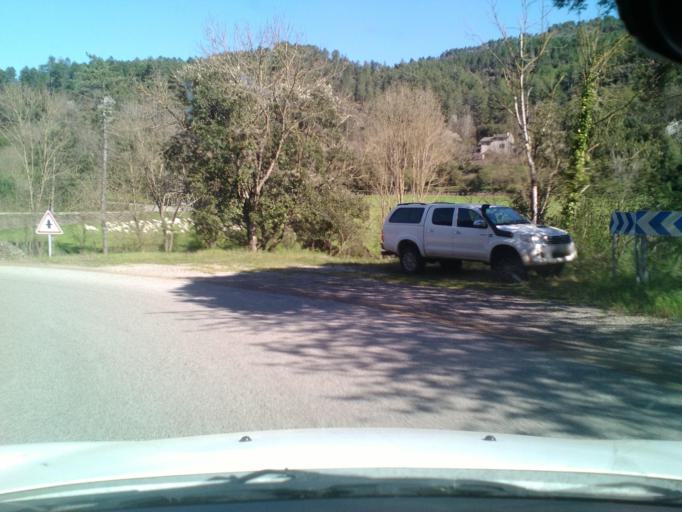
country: FR
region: Languedoc-Roussillon
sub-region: Departement du Gard
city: Saint-Jean-du-Gard
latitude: 44.1699
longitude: 3.7644
